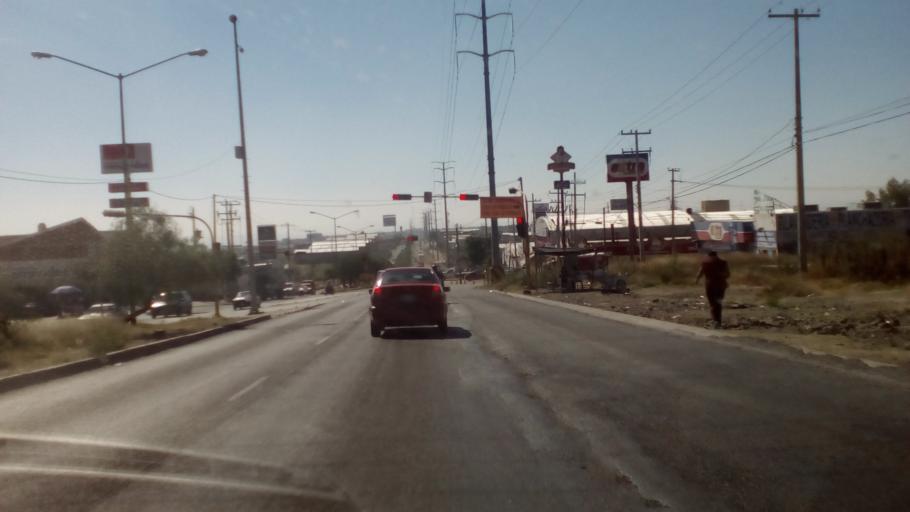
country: MX
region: Guanajuato
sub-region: Leon
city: La Ermita
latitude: 21.1530
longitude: -101.7300
